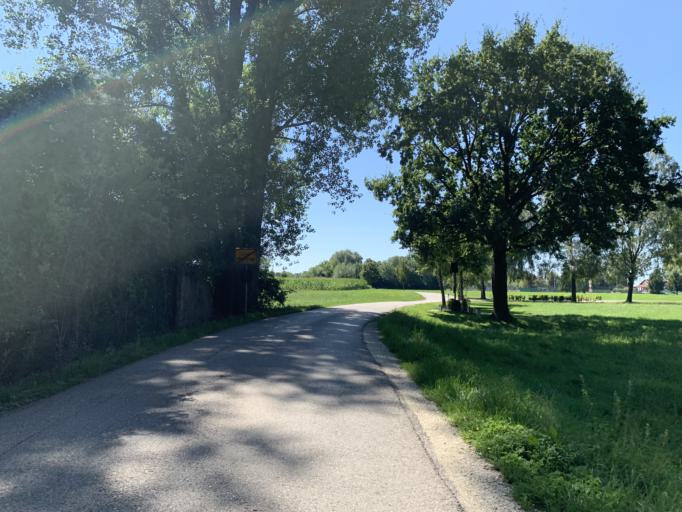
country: DE
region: Bavaria
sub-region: Upper Bavaria
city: Freising
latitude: 48.3915
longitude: 11.7222
